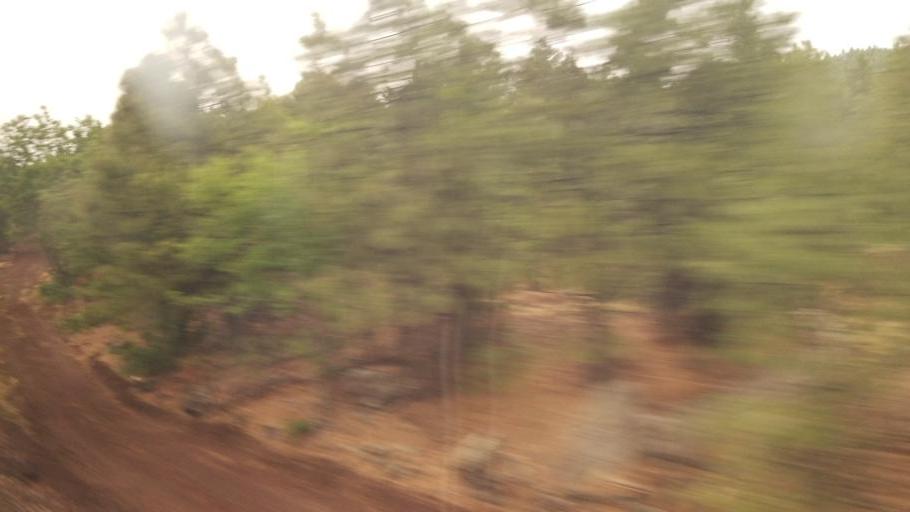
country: US
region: Arizona
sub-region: Coconino County
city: Parks
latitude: 35.2548
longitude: -111.9264
